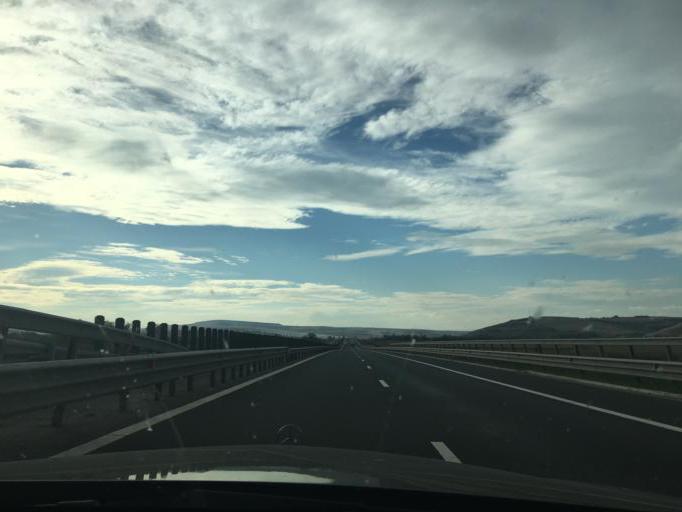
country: RO
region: Sibiu
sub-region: Oras Miercurea Sibiului
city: Miercurea Sibiului
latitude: 45.8969
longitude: 23.7993
